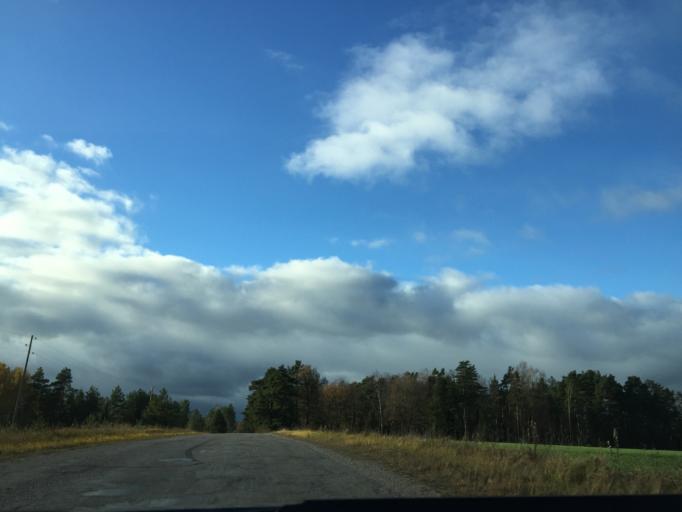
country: LV
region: Kandava
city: Kandava
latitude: 56.9692
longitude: 22.9447
